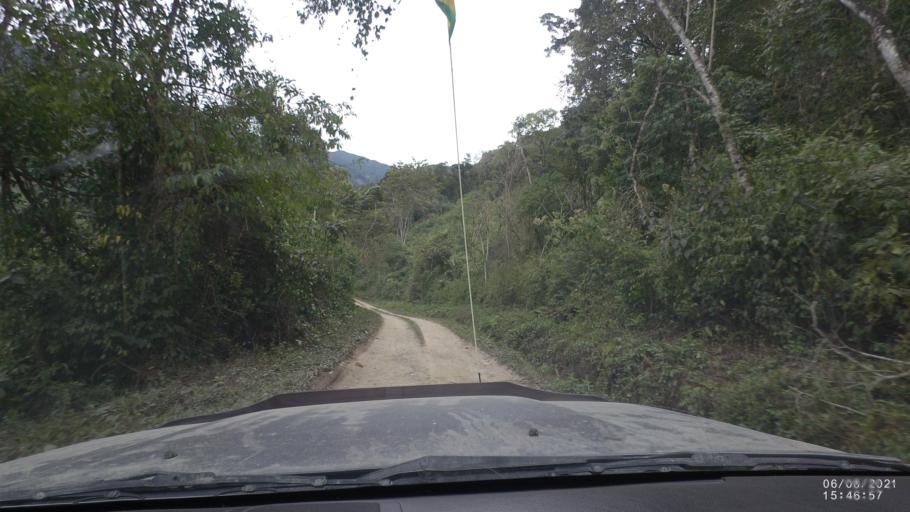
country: BO
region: La Paz
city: Quime
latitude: -16.5940
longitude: -66.7066
